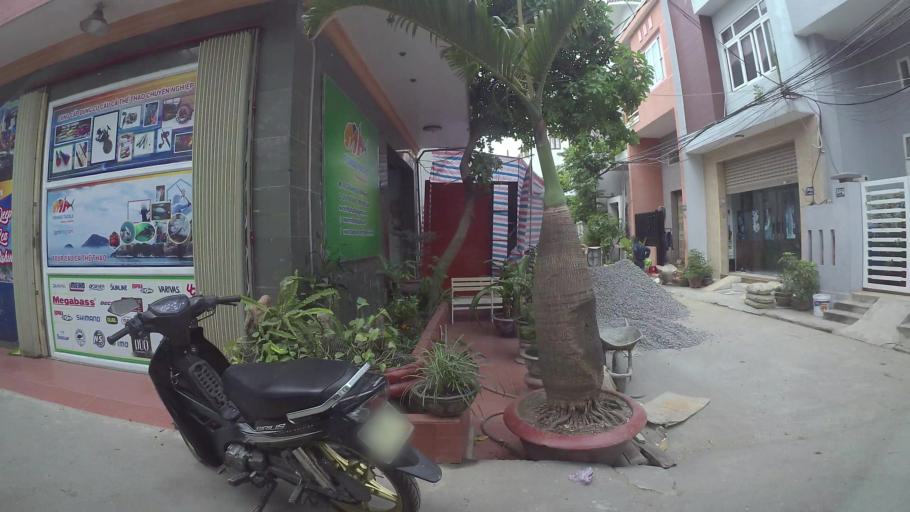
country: VN
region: Da Nang
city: Da Nang
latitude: 16.0850
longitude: 108.2218
